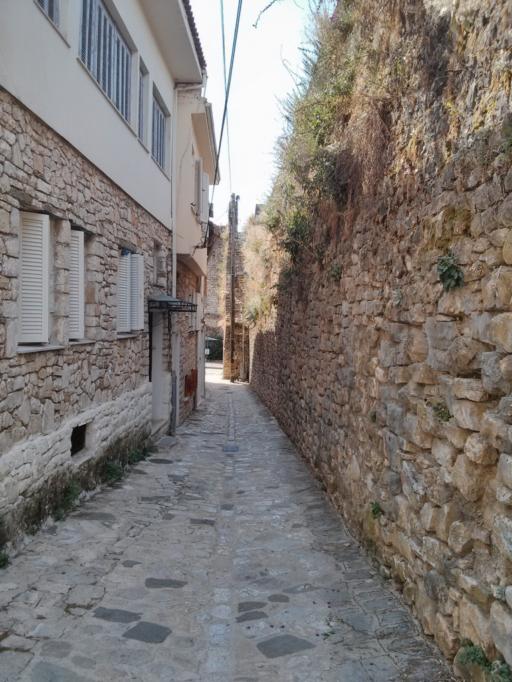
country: GR
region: Epirus
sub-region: Nomos Ioanninon
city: Ioannina
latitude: 39.6708
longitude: 20.8579
